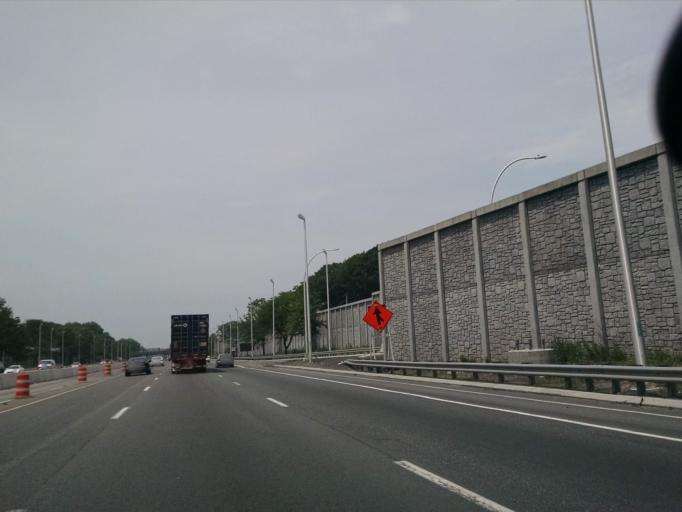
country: US
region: New York
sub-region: Richmond County
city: Bloomfield
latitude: 40.6081
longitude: -74.1342
